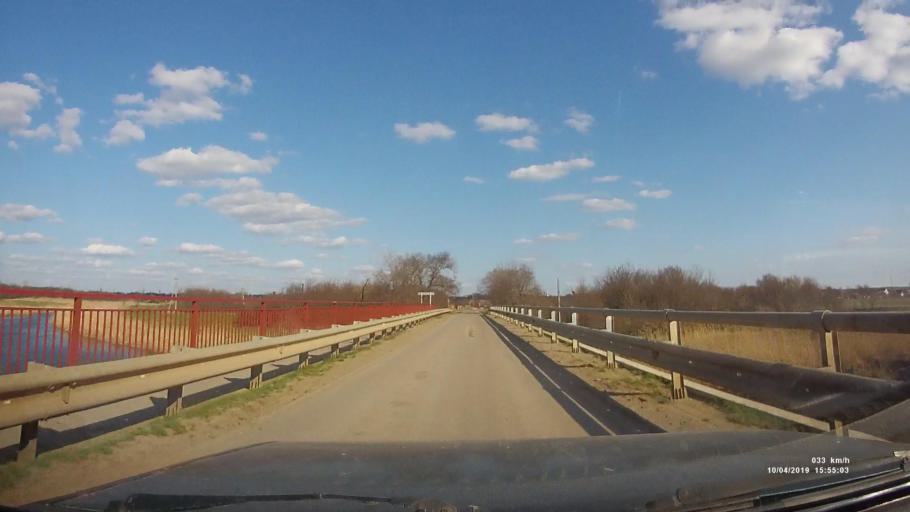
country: RU
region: Rostov
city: Masalovka
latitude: 48.4136
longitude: 40.2619
